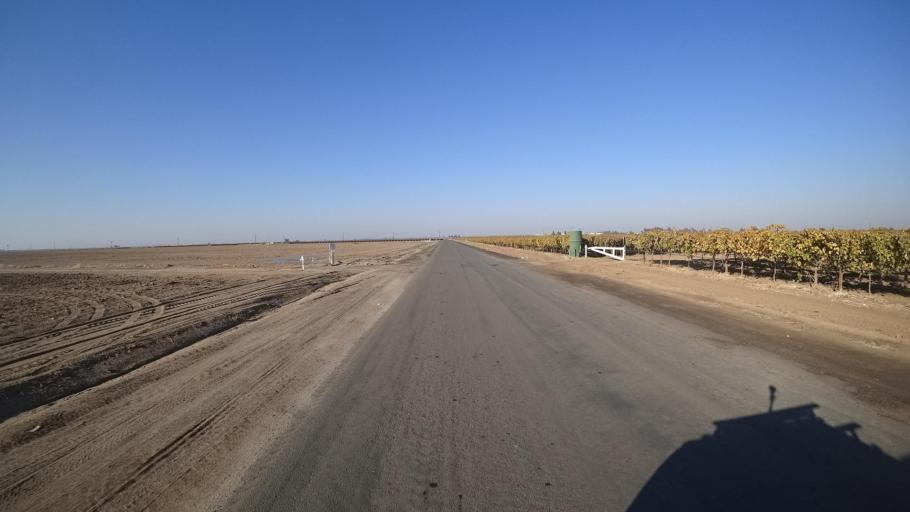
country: US
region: California
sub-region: Tulare County
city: Richgrove
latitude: 35.7687
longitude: -119.1650
